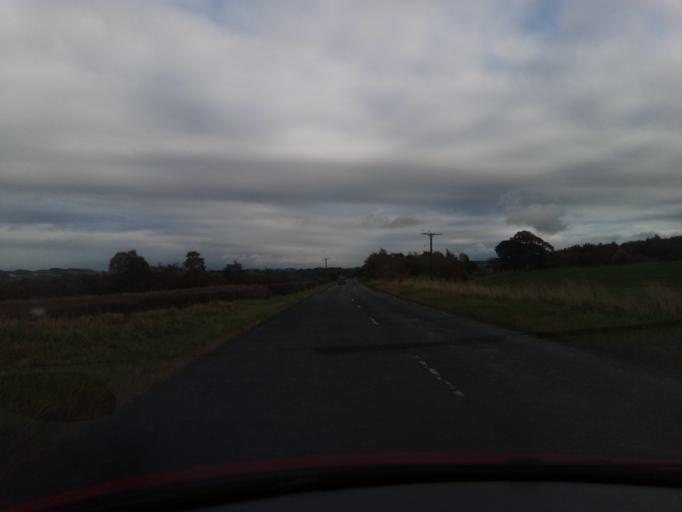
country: GB
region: Scotland
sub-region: The Scottish Borders
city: Newtown St Boswells
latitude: 55.5667
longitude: -2.6680
